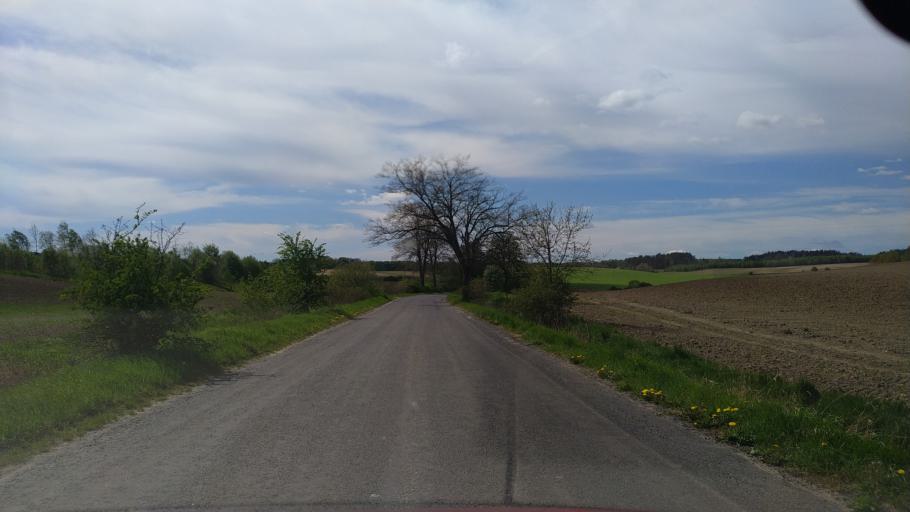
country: PL
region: West Pomeranian Voivodeship
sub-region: Powiat walecki
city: Walcz
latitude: 53.3534
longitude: 16.3098
